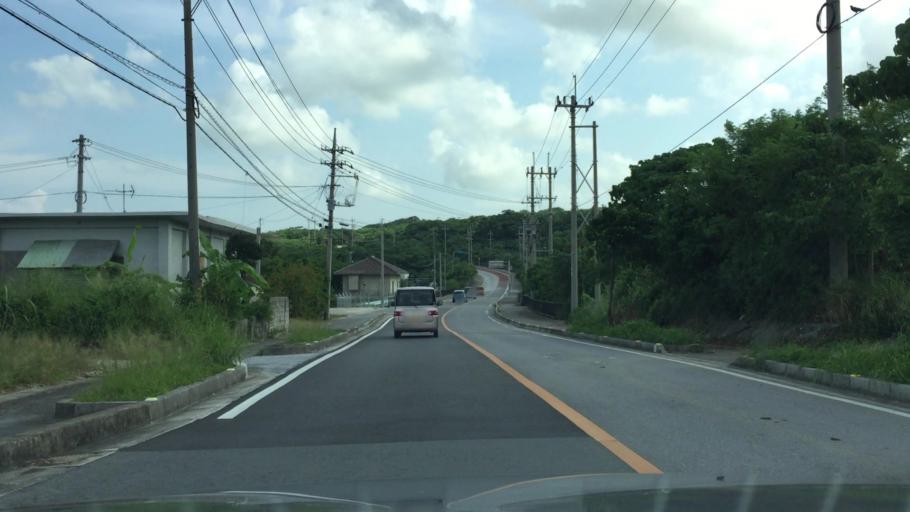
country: JP
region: Okinawa
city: Ishigaki
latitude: 24.4339
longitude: 124.2485
